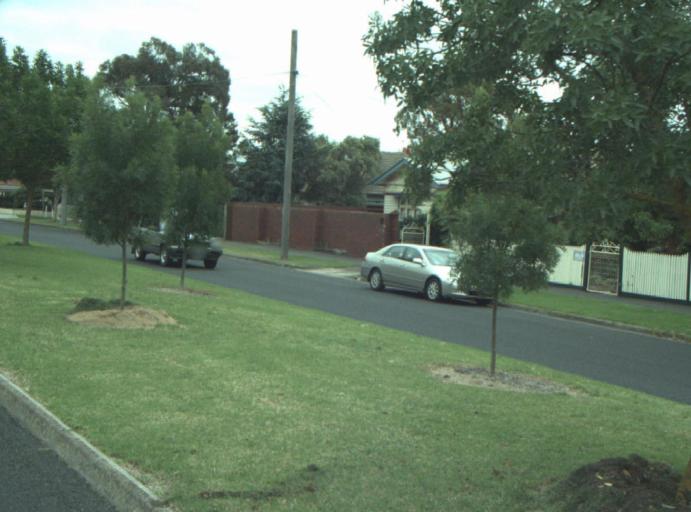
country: AU
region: Victoria
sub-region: Greater Geelong
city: East Geelong
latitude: -38.1577
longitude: 144.3809
